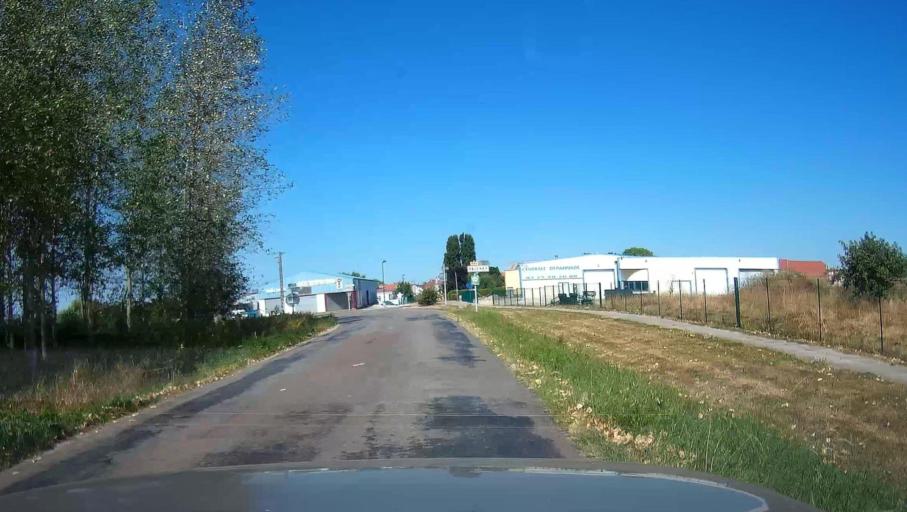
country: FR
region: Champagne-Ardenne
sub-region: Departement de la Haute-Marne
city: Langres
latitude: 47.8792
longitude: 5.3690
